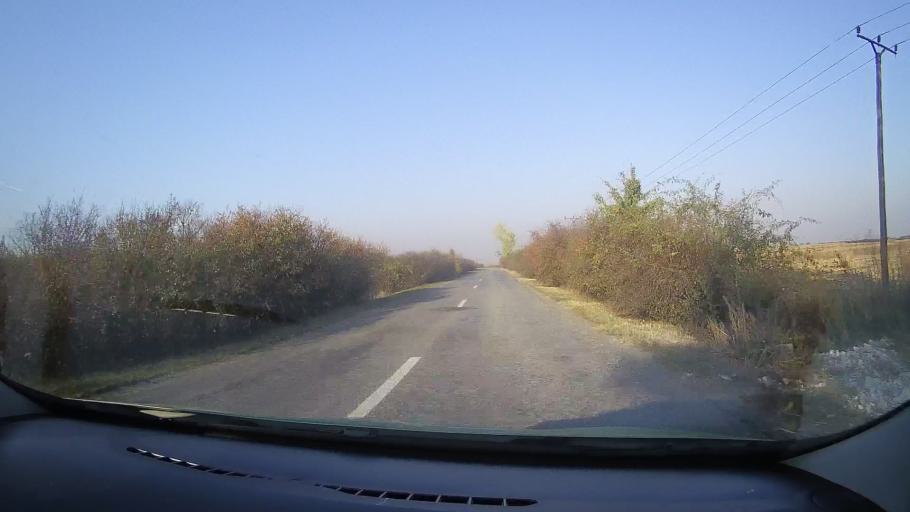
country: RO
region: Arad
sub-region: Comuna Socodor
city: Socodor
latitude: 46.5034
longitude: 21.4125
